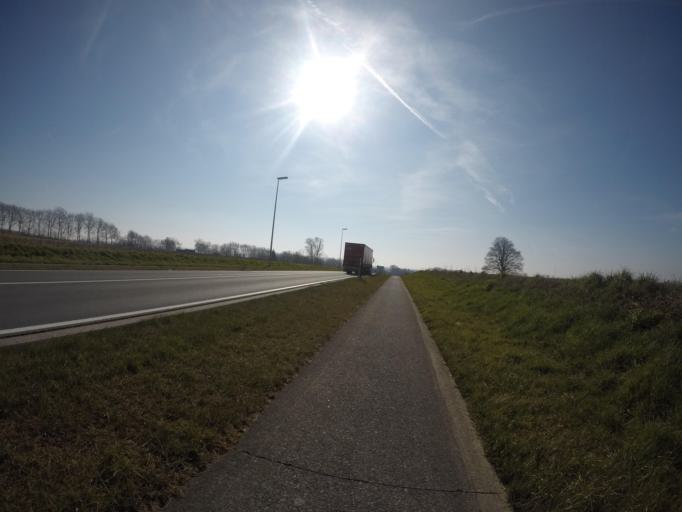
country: BE
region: Flanders
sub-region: Provincie Oost-Vlaanderen
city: Sint-Maria-Lierde
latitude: 50.8103
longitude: 3.8711
